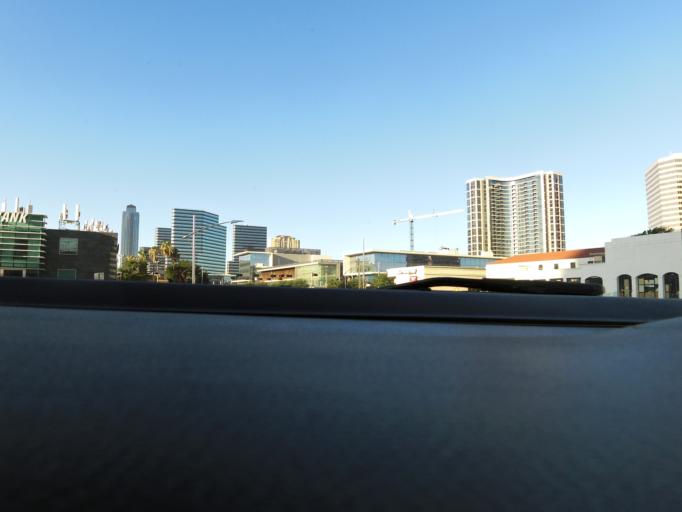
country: US
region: Texas
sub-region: Harris County
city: Hunters Creek Village
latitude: 29.7515
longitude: -95.4608
